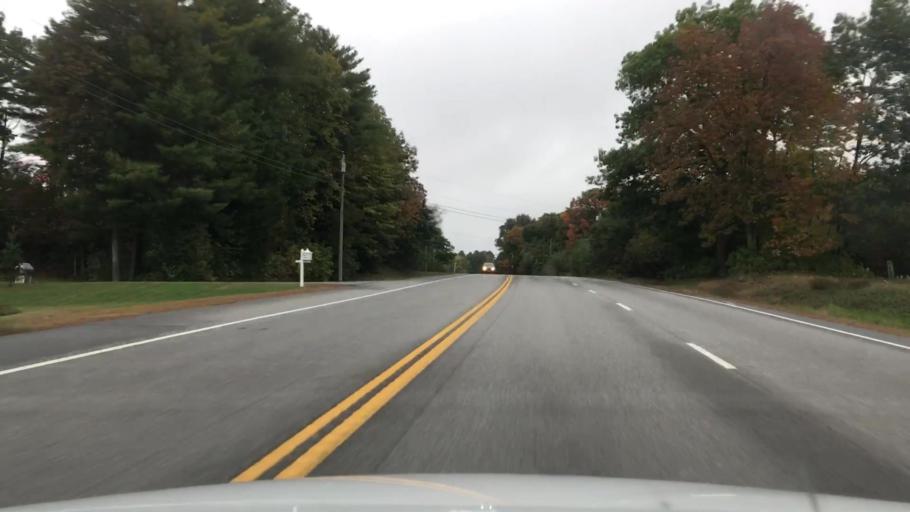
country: US
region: Maine
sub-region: Androscoggin County
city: Poland
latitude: 44.0854
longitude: -70.4200
